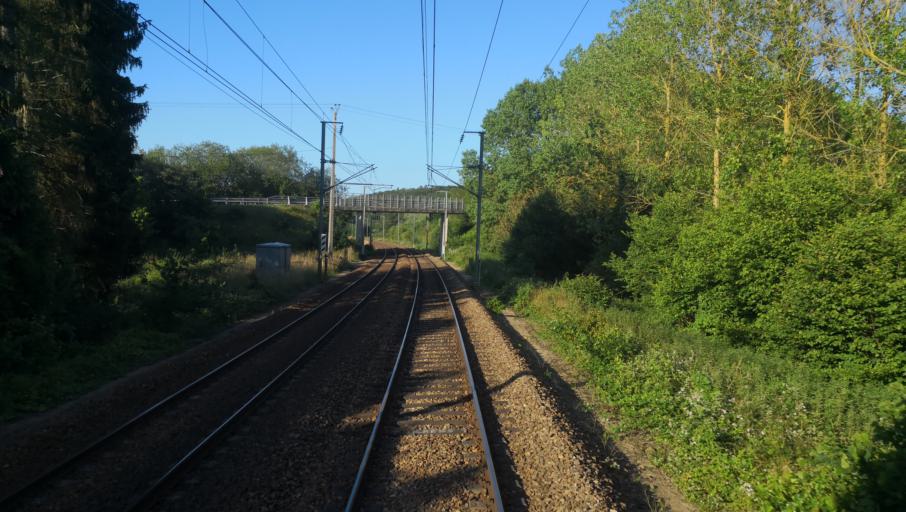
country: FR
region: Haute-Normandie
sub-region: Departement de l'Eure
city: Serquigny
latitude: 49.0924
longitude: 0.6891
